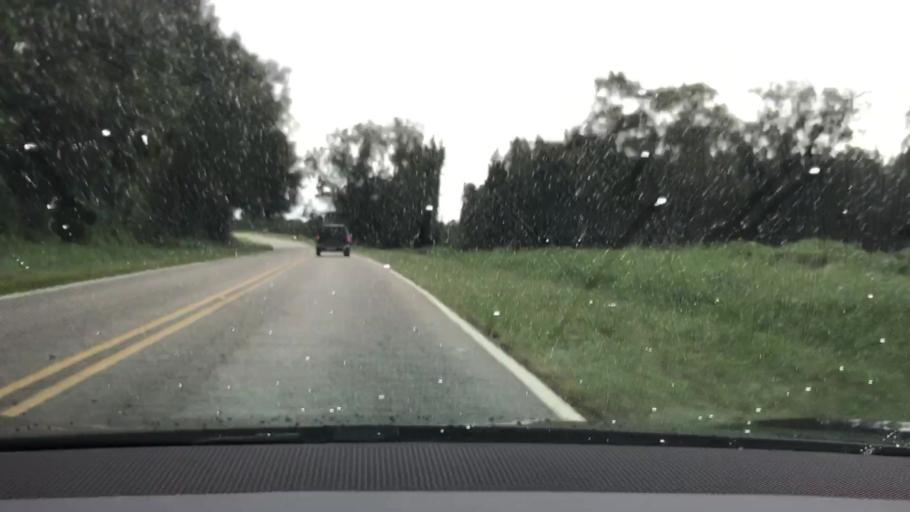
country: US
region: Alabama
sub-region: Geneva County
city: Samson
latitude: 31.1340
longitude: -86.1347
